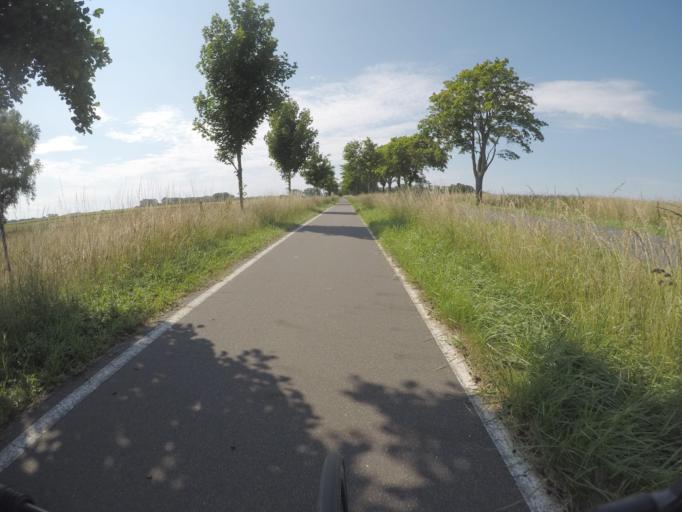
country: DE
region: Mecklenburg-Vorpommern
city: Gingst
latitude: 54.4439
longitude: 13.2096
